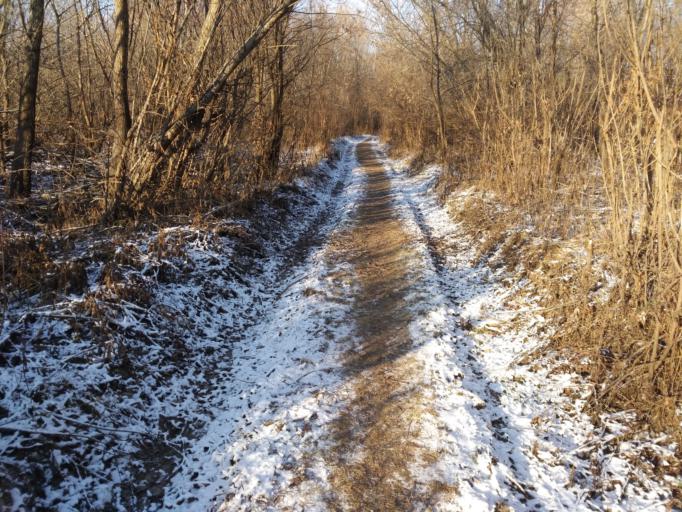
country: RU
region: Kirov
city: Vyatskiye Polyany
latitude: 56.2357
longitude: 51.0792
